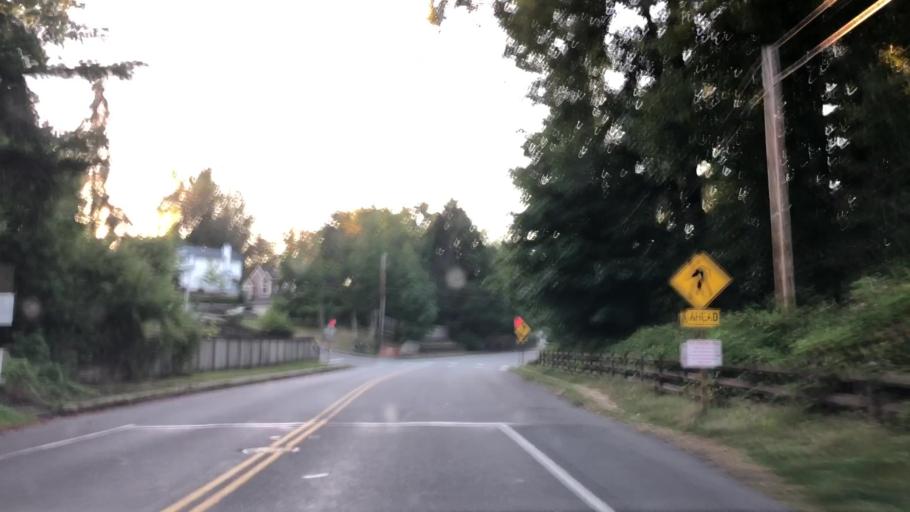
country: US
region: Washington
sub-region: Snohomish County
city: Brier
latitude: 47.7771
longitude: -122.2709
